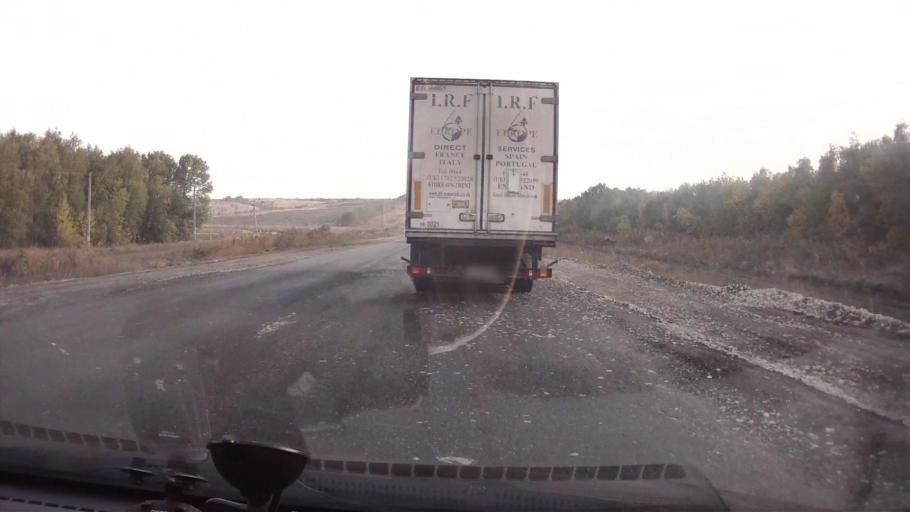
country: RU
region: Saratov
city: Krasnyy Oktyabr'
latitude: 51.3441
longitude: 45.7130
